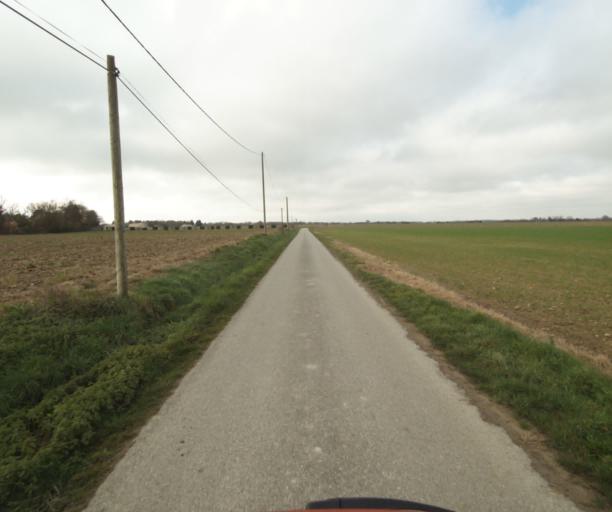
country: FR
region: Languedoc-Roussillon
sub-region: Departement de l'Aude
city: Belpech
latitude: 43.1784
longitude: 1.7200
